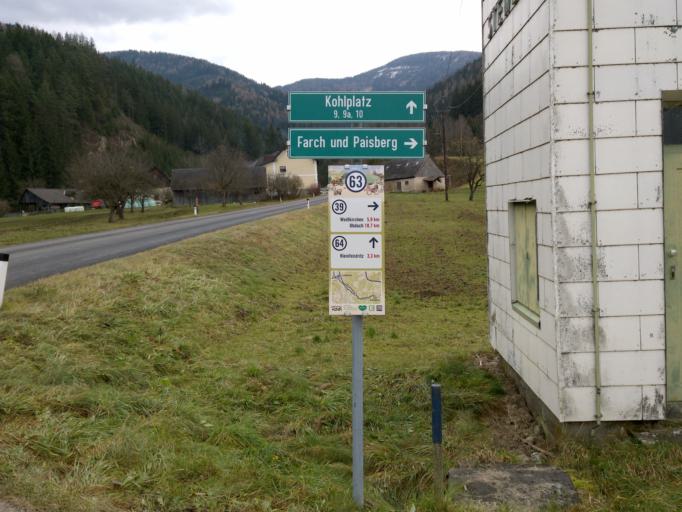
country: AT
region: Styria
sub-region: Politischer Bezirk Murtal
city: Kleinlobming
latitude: 47.1392
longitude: 14.7956
